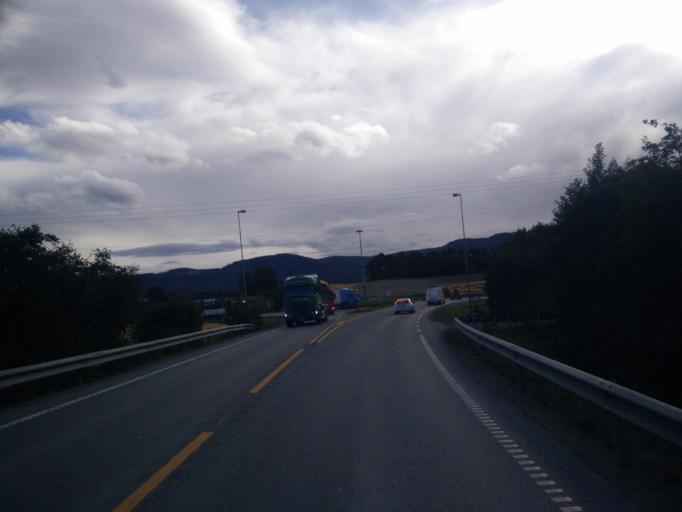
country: NO
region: Sor-Trondelag
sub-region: Melhus
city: Melhus
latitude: 63.3231
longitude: 10.3019
